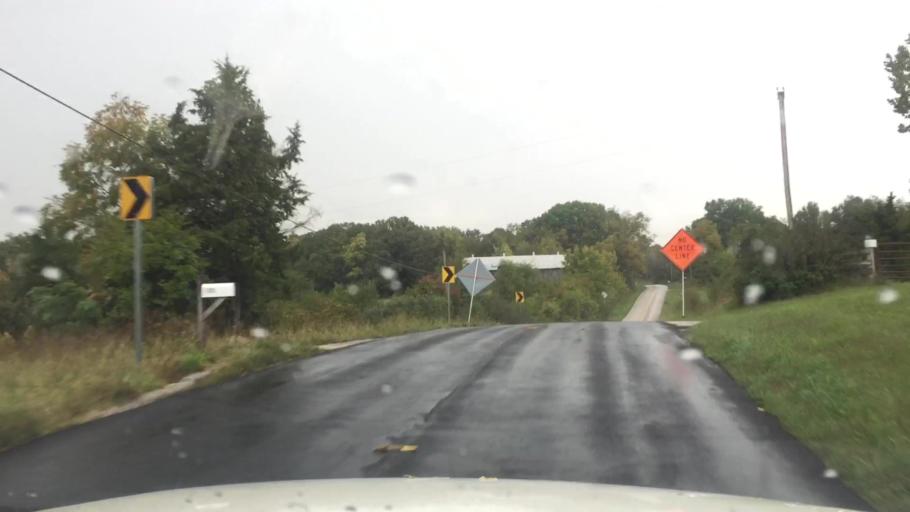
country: US
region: Missouri
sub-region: Boone County
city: Columbia
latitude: 38.9432
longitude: -92.4966
